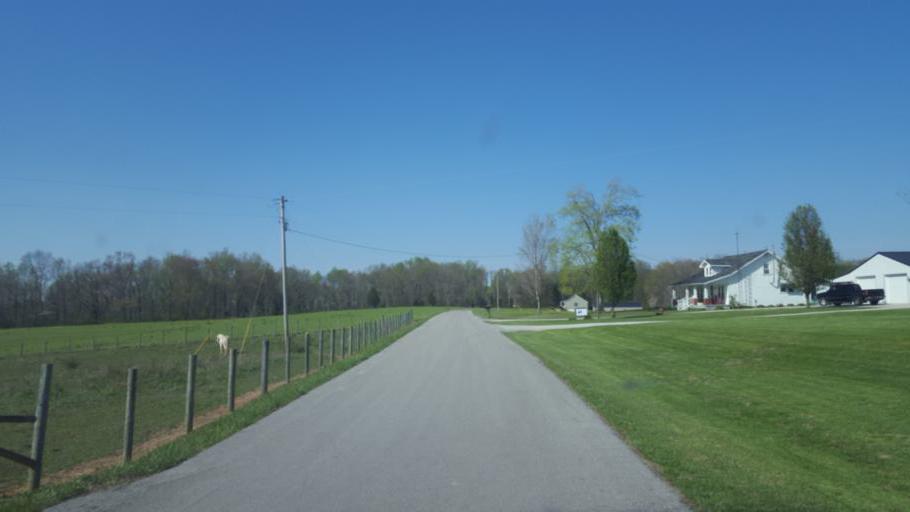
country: US
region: Kentucky
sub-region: Edmonson County
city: Brownsville
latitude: 37.1398
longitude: -86.1625
